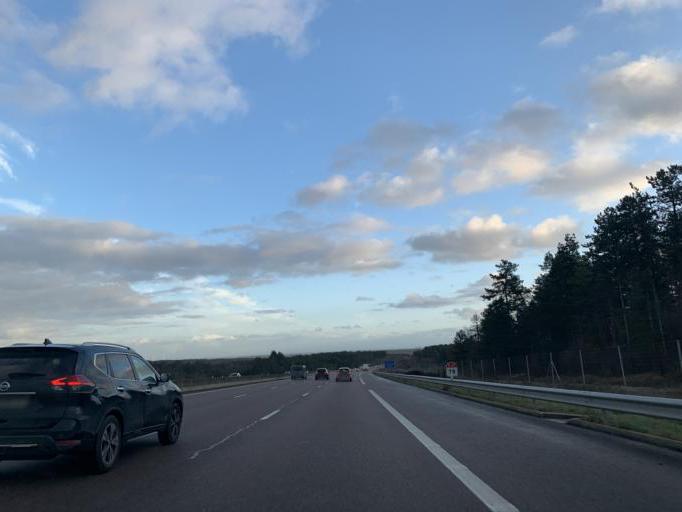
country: FR
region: Bourgogne
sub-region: Departement de la Cote-d'Or
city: Selongey
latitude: 47.6067
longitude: 5.1948
